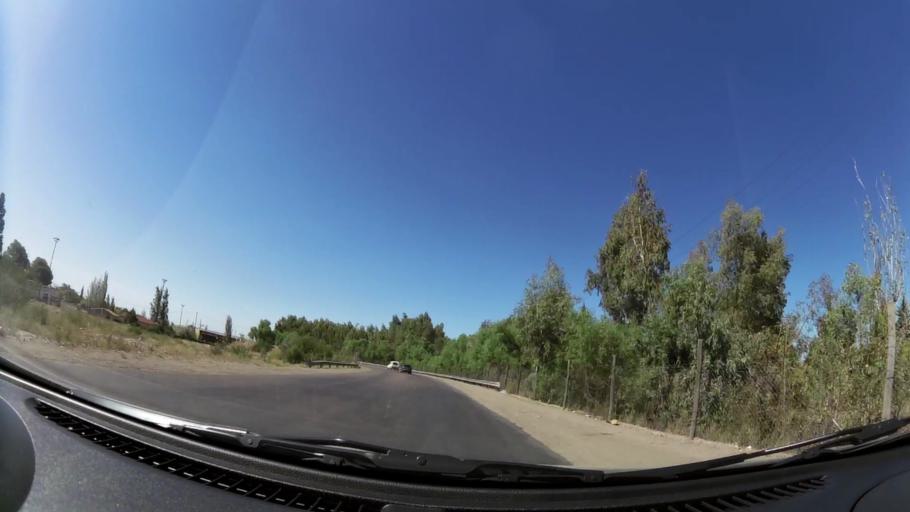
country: AR
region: Mendoza
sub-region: Departamento de Godoy Cruz
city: Godoy Cruz
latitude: -32.9707
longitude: -68.8347
